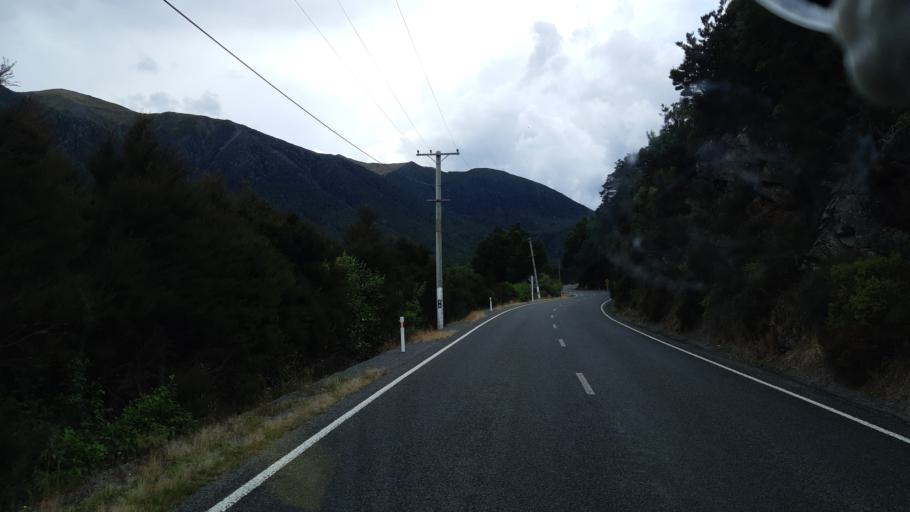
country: NZ
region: Canterbury
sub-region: Hurunui District
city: Amberley
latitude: -42.5502
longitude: 172.3473
